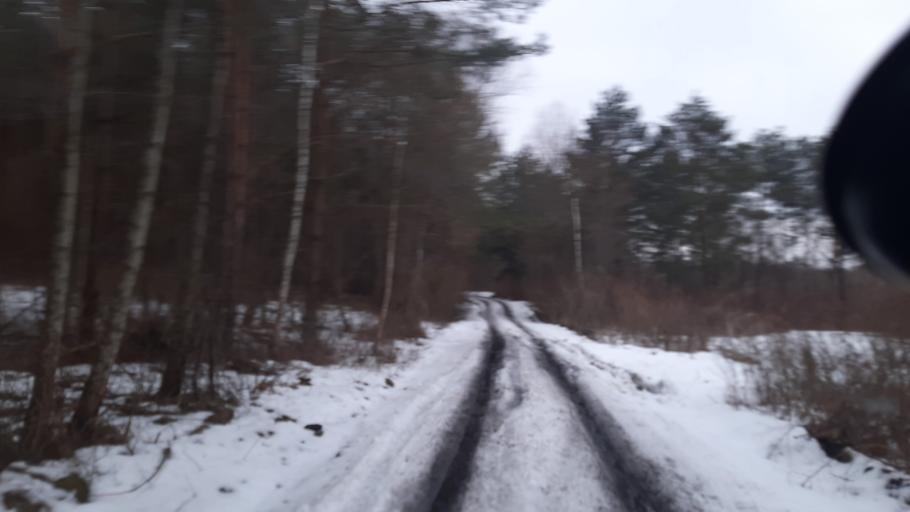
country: PL
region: Lublin Voivodeship
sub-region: Powiat wlodawski
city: Wlodawa
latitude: 51.5121
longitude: 23.6126
